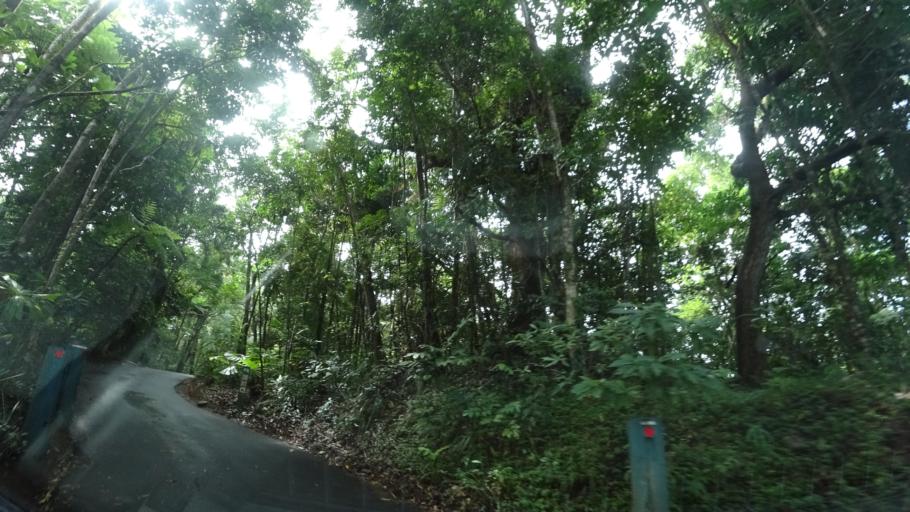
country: AU
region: Queensland
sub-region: Cairns
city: Port Douglas
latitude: -16.2457
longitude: 145.4352
